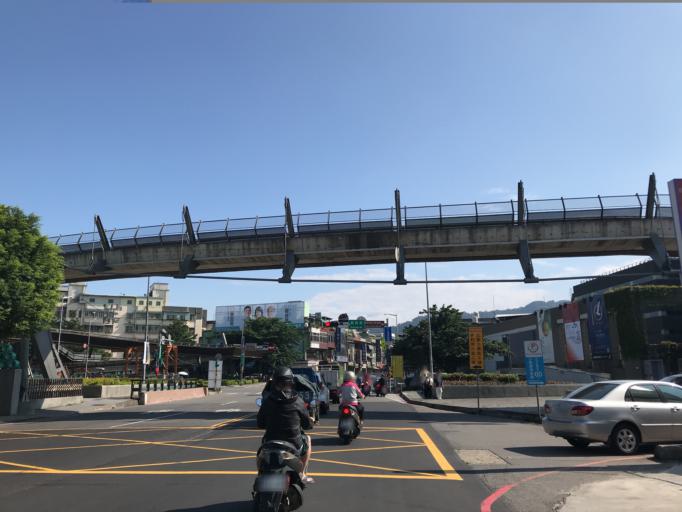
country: TW
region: Taiwan
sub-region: Taoyuan
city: Taoyuan
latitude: 24.9503
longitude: 121.3524
